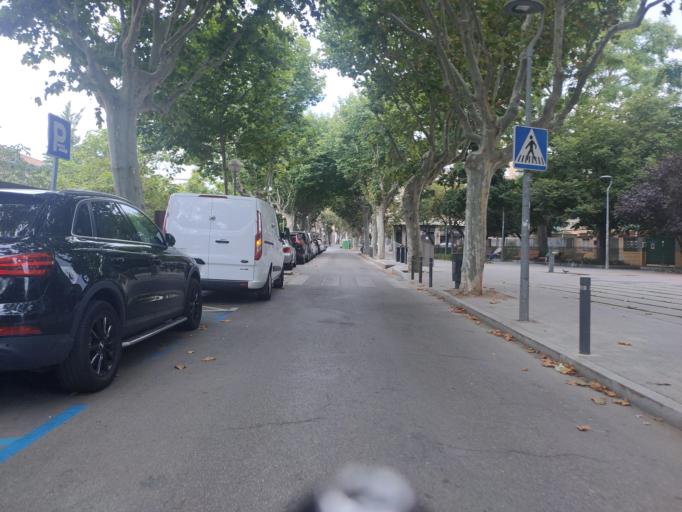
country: ES
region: Catalonia
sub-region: Provincia de Barcelona
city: Mollet del Valles
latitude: 41.5379
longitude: 2.2103
